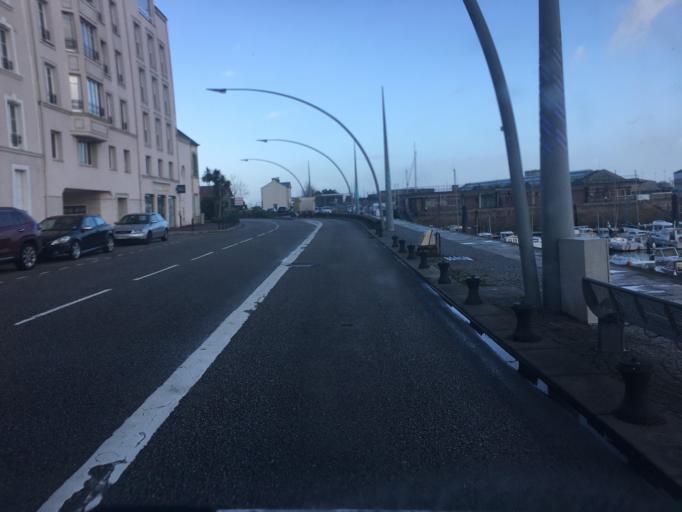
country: FR
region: Lower Normandy
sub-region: Departement de la Manche
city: Cherbourg-Octeville
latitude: 49.6408
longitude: -1.6213
